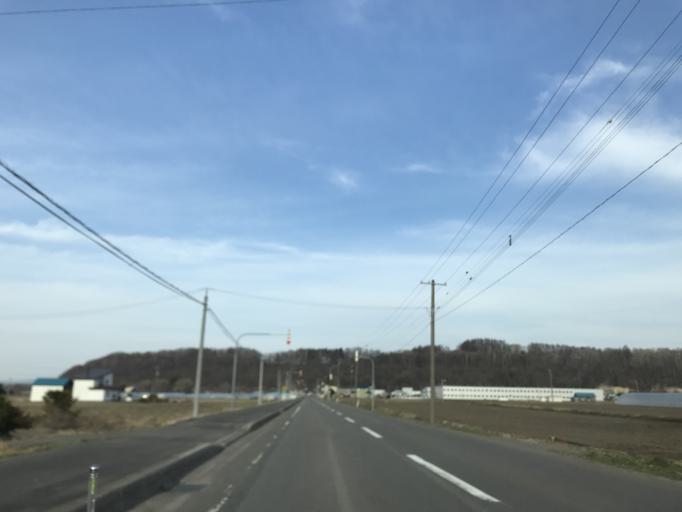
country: JP
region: Hokkaido
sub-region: Asahikawa-shi
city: Asahikawa
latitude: 43.7069
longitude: 142.3488
